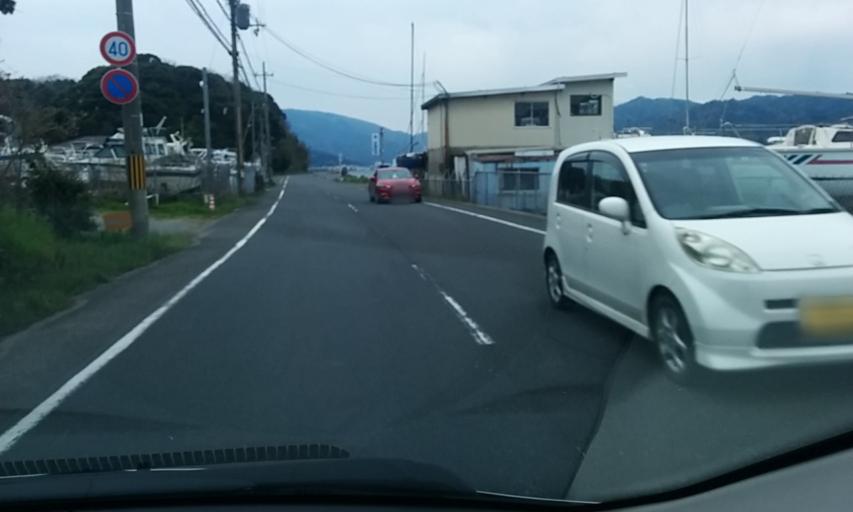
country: JP
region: Kyoto
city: Miyazu
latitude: 35.5593
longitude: 135.2049
